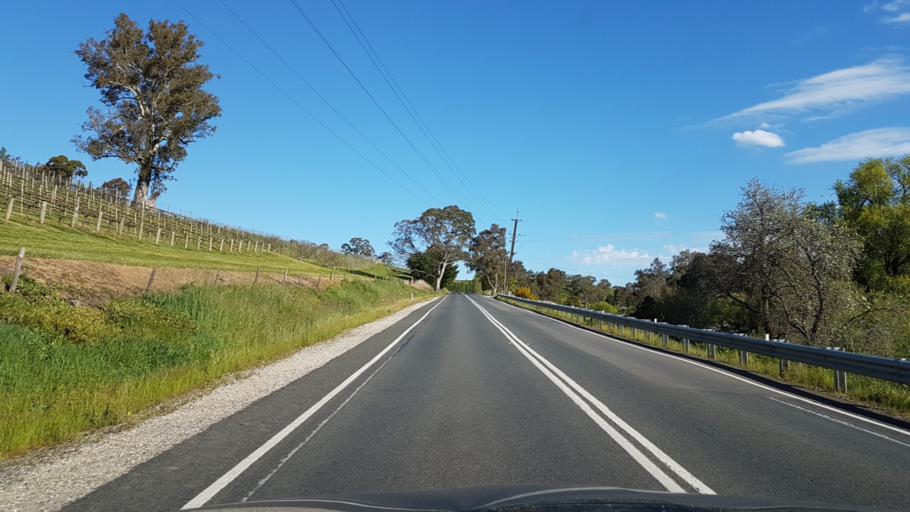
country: AU
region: South Australia
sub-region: Adelaide Hills
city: Gumeracha
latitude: -34.8375
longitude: 138.8929
